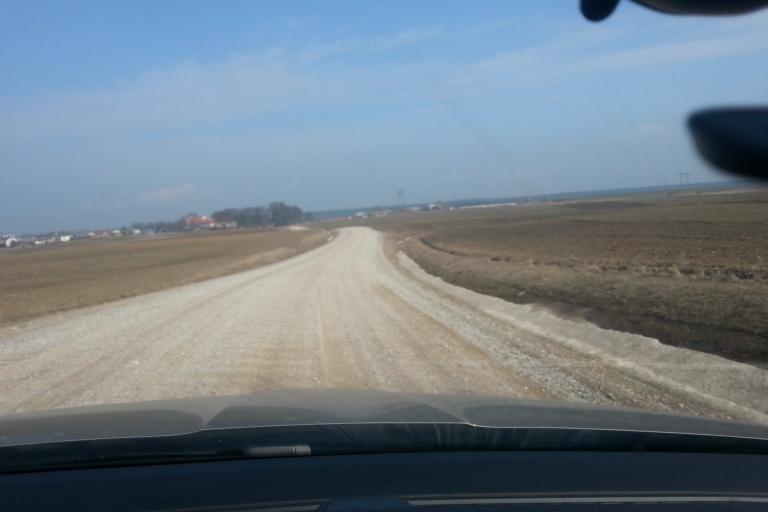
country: LT
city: Trakai
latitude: 54.5987
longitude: 24.9790
